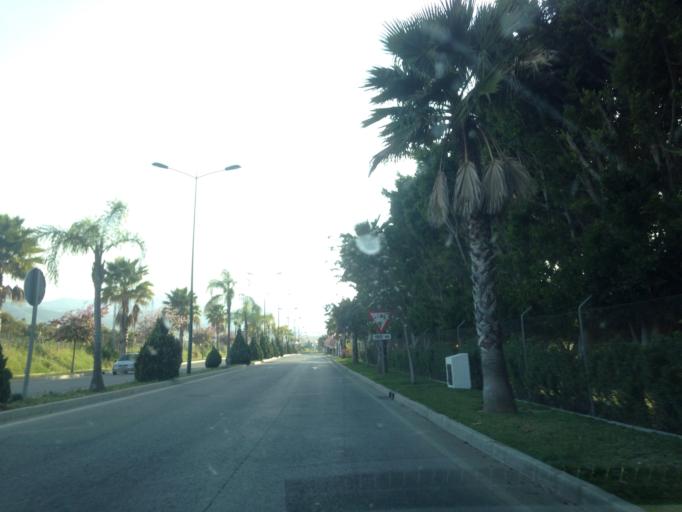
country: ES
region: Andalusia
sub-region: Provincia de Malaga
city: Alhaurin de la Torre
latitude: 36.6819
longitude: -4.5384
